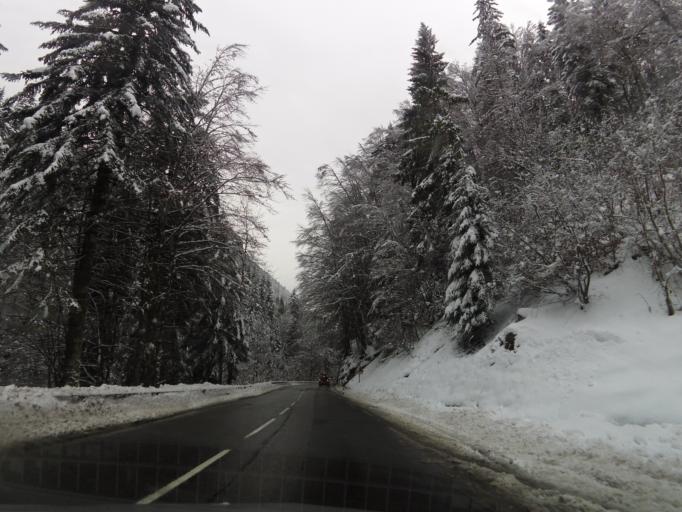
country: FR
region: Rhone-Alpes
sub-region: Departement de la Haute-Savoie
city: Les Gets
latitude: 46.1378
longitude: 6.6356
